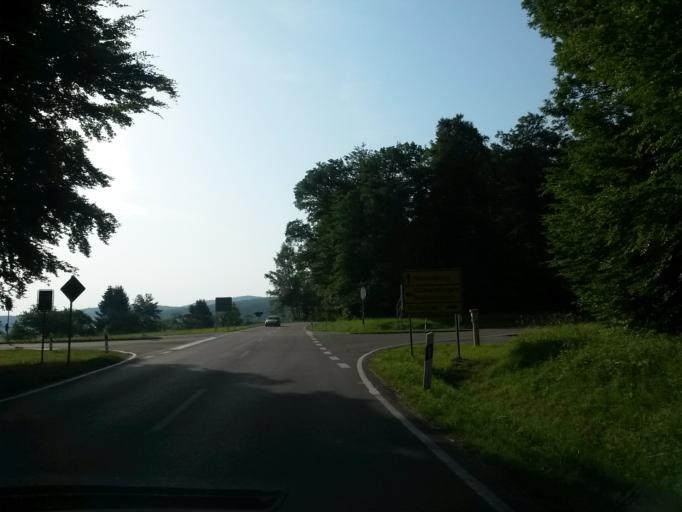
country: DE
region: Baden-Wuerttemberg
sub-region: Karlsruhe Region
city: Neuenburg
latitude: 48.8656
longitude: 8.5564
